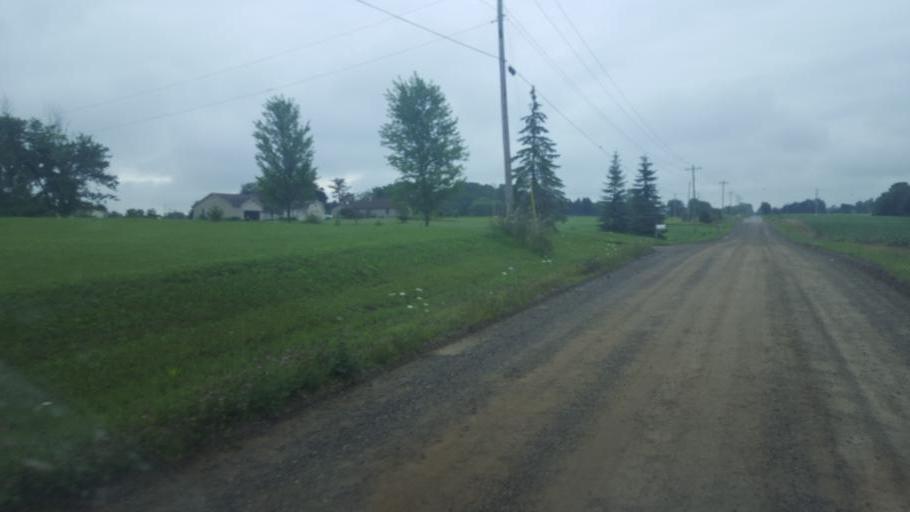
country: US
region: Ohio
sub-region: Knox County
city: Centerburg
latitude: 40.4219
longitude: -82.7413
